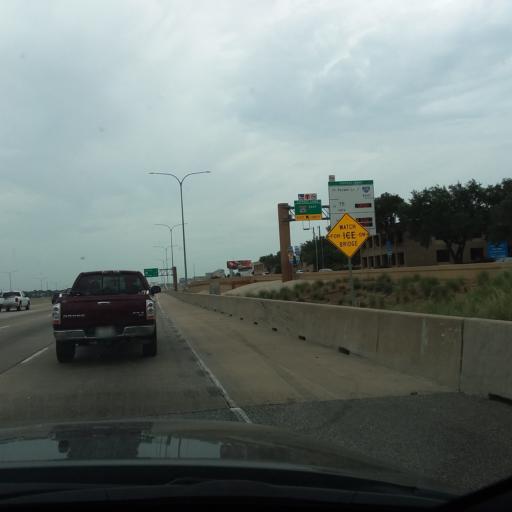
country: US
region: Texas
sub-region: Dallas County
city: Addison
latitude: 32.9247
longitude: -96.7975
